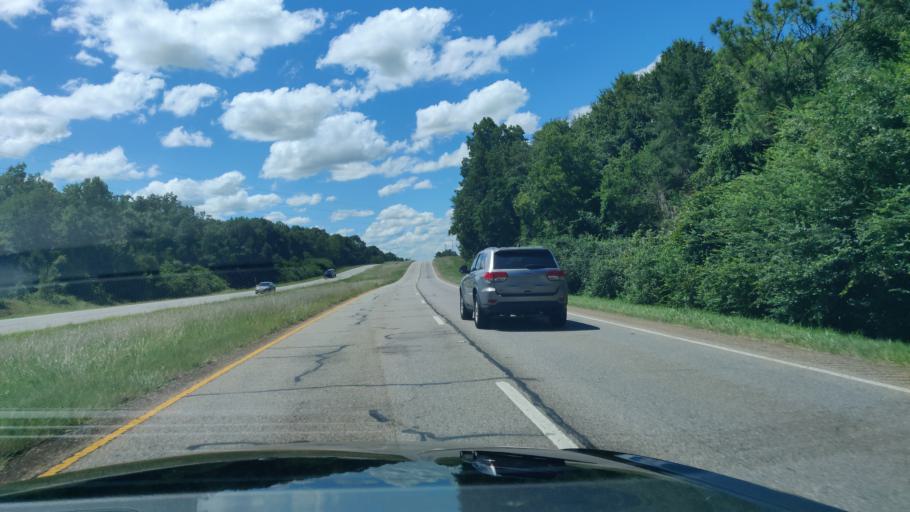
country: US
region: Georgia
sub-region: Webster County
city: Preston
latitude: 31.9248
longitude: -84.5524
